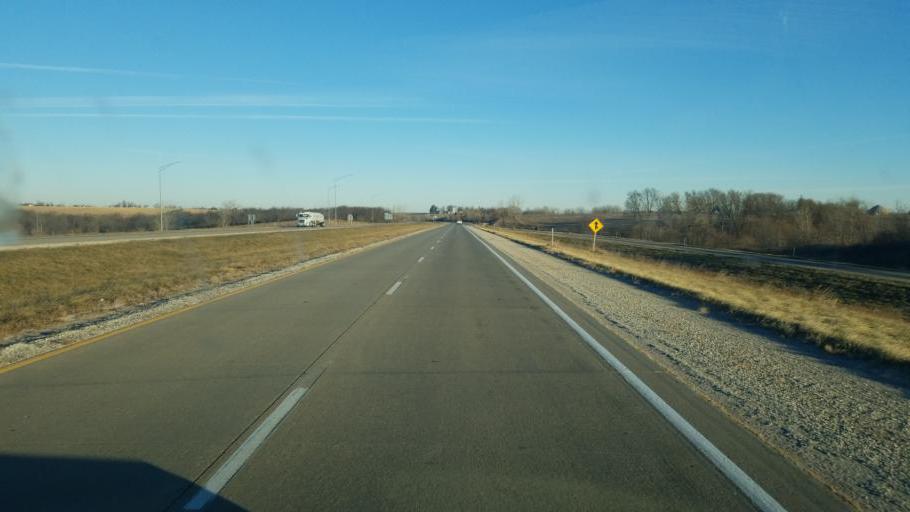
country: US
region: Iowa
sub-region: Mahaska County
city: Oskaloosa
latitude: 41.2980
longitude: -92.6746
